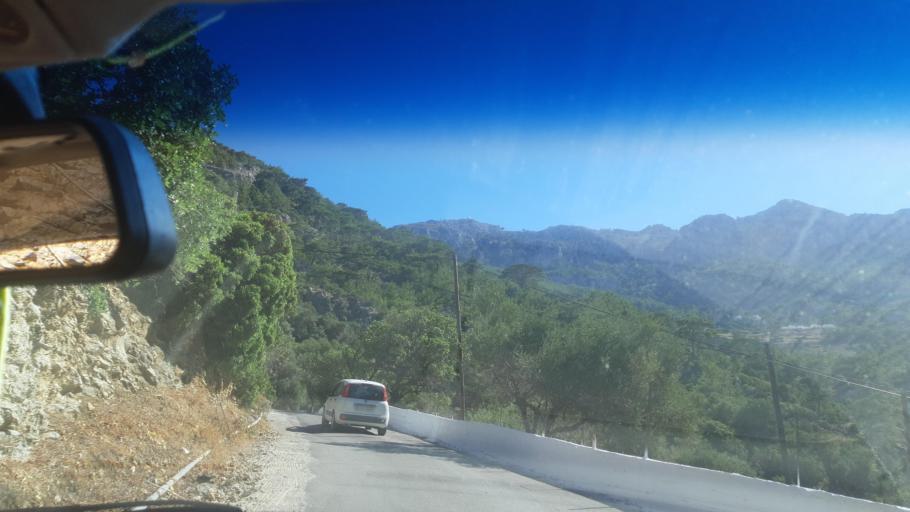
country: GR
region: South Aegean
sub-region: Nomos Dodekanisou
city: Karpathos
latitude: 35.5860
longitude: 27.1774
